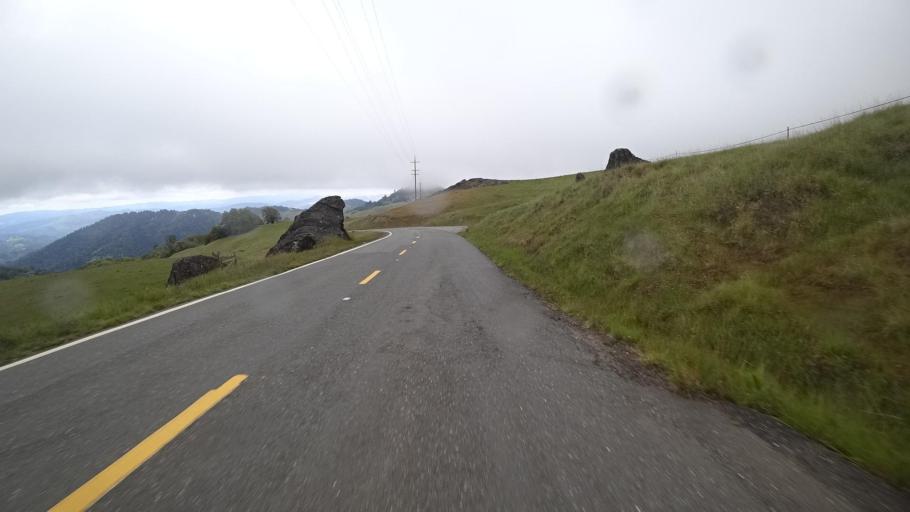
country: US
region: California
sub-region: Humboldt County
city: Redway
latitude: 40.1049
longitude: -123.7107
